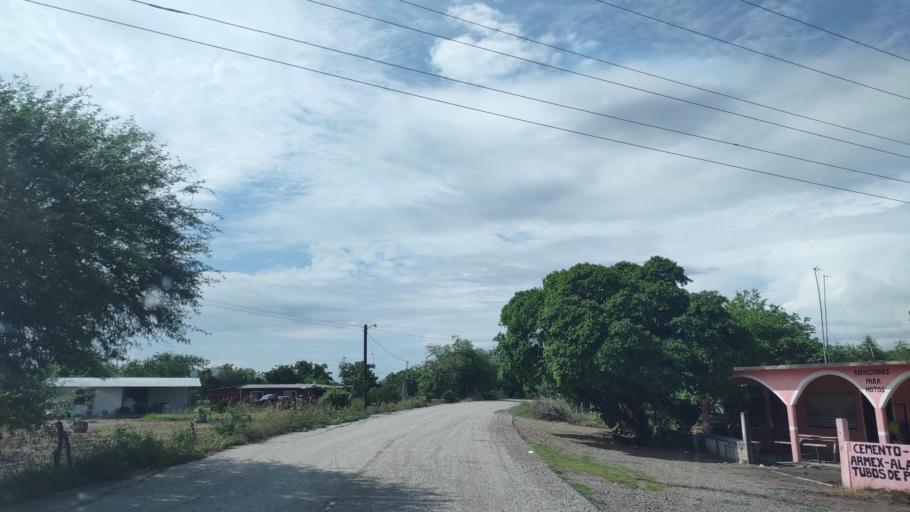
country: MX
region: Veracruz
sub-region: Panuco
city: Oviedo
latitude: 22.0040
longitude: -98.4613
